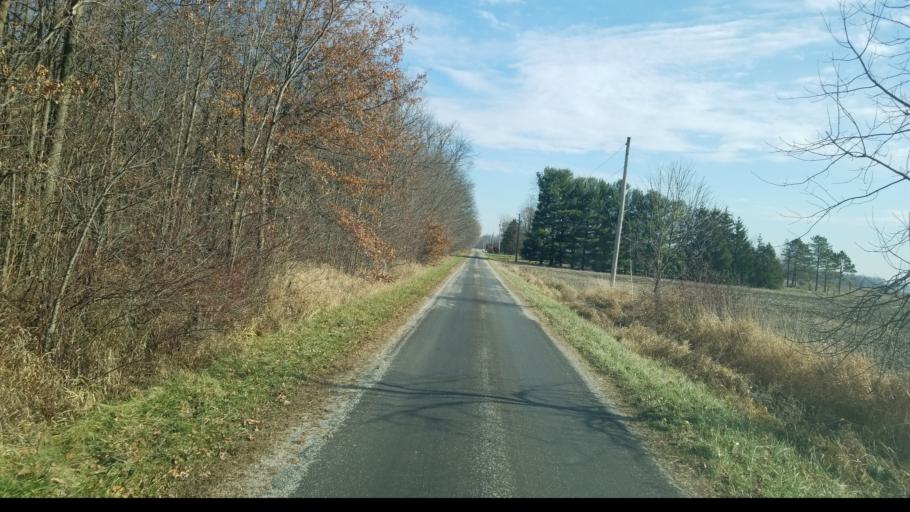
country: US
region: Ohio
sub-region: Morrow County
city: Cardington
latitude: 40.6089
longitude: -82.9481
